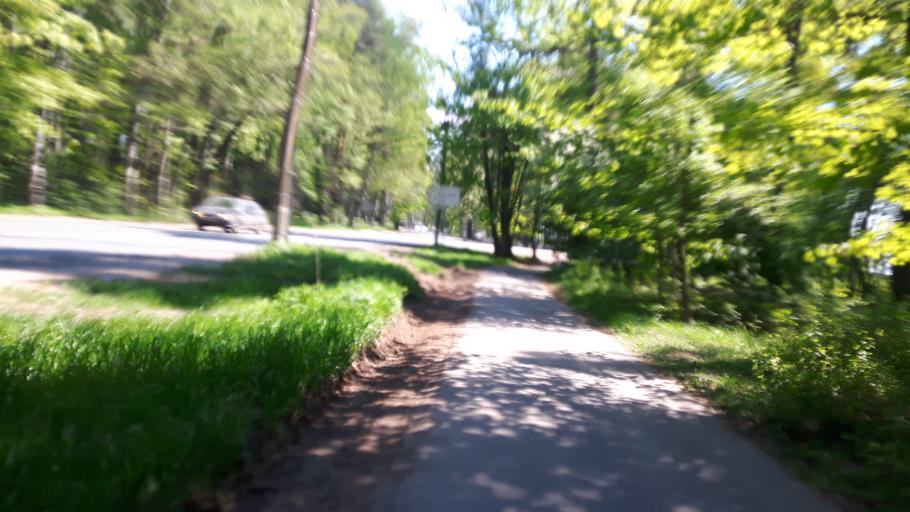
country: RU
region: St.-Petersburg
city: Komarovo
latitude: 60.1695
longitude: 29.8178
